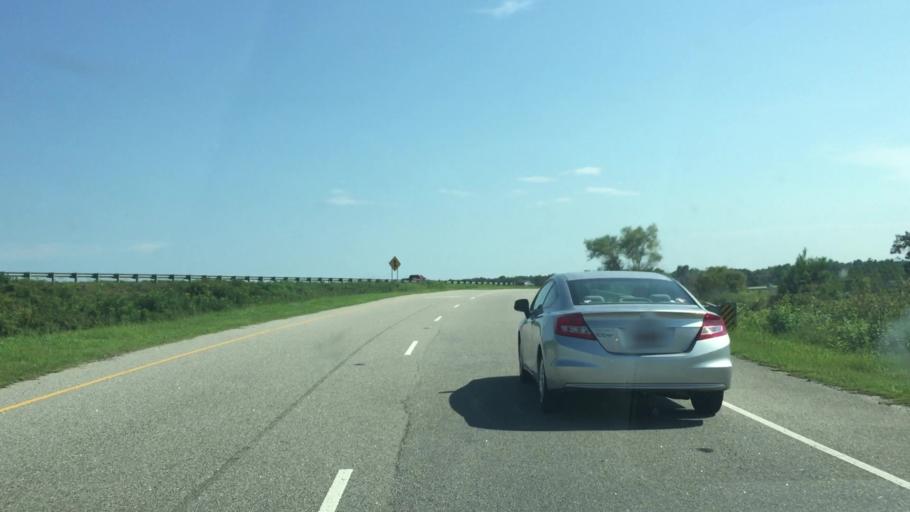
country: US
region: South Carolina
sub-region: Horry County
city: North Myrtle Beach
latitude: 33.8435
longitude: -78.7025
